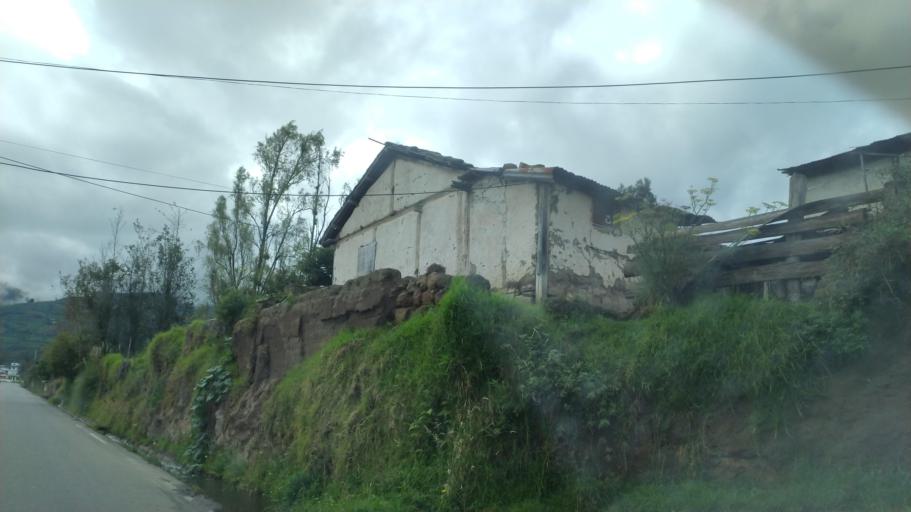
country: EC
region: Chimborazo
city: Riobamba
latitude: -1.6595
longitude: -78.5767
